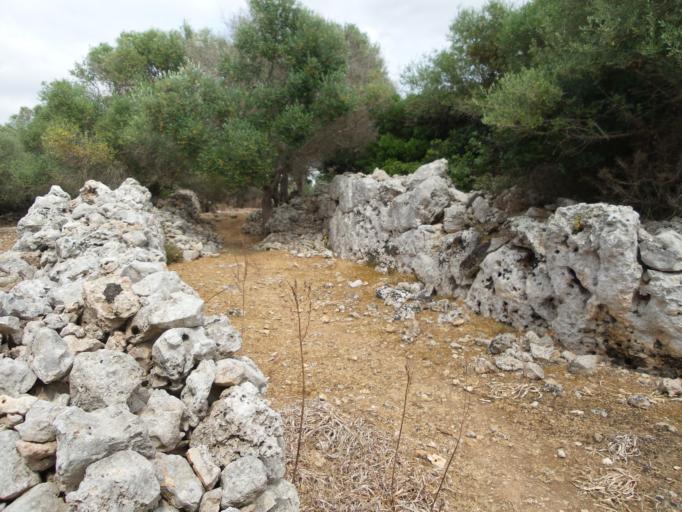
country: ES
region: Balearic Islands
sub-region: Illes Balears
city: Ciutadella
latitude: 39.9533
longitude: 3.8756
